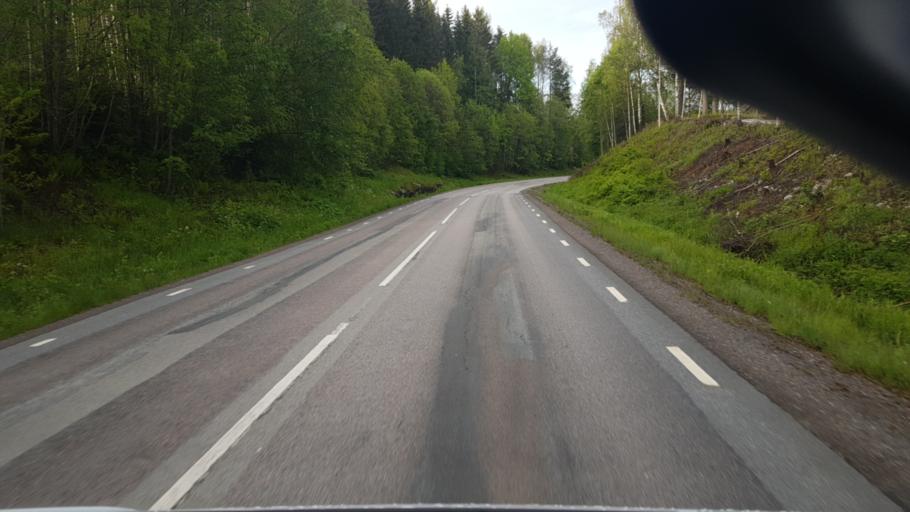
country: SE
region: Vaermland
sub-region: Eda Kommun
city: Charlottenberg
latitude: 59.8411
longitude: 12.2830
